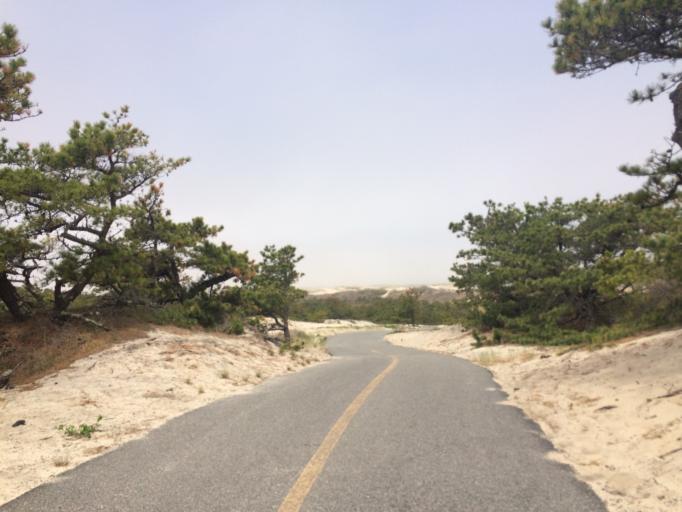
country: US
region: Massachusetts
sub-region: Barnstable County
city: Provincetown
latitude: 42.0741
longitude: -70.2020
